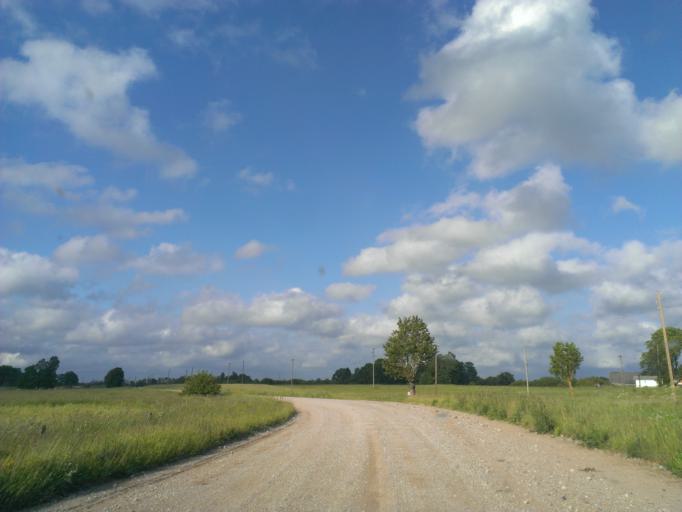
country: LV
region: Aizpute
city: Aizpute
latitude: 56.7553
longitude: 21.4542
